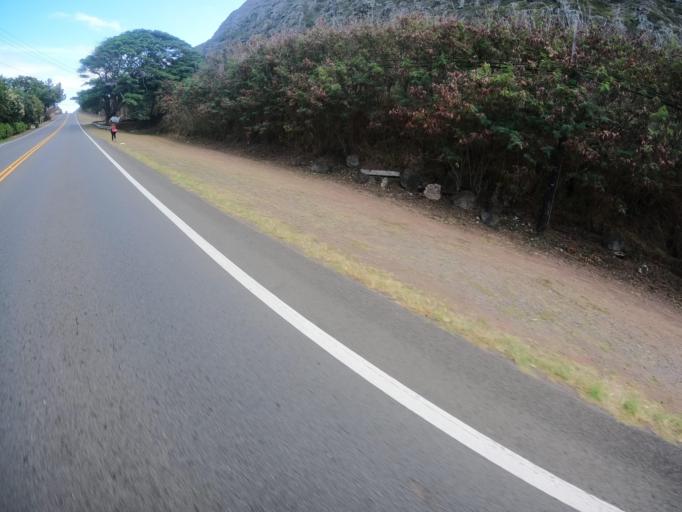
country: US
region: Hawaii
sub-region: Honolulu County
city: Waimanalo Beach
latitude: 21.3228
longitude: -157.6772
